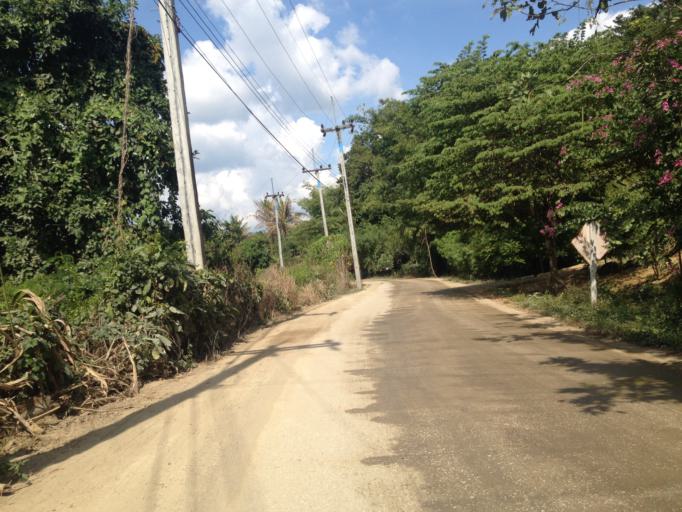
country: TH
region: Chiang Mai
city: Hang Dong
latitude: 18.6925
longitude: 98.8741
